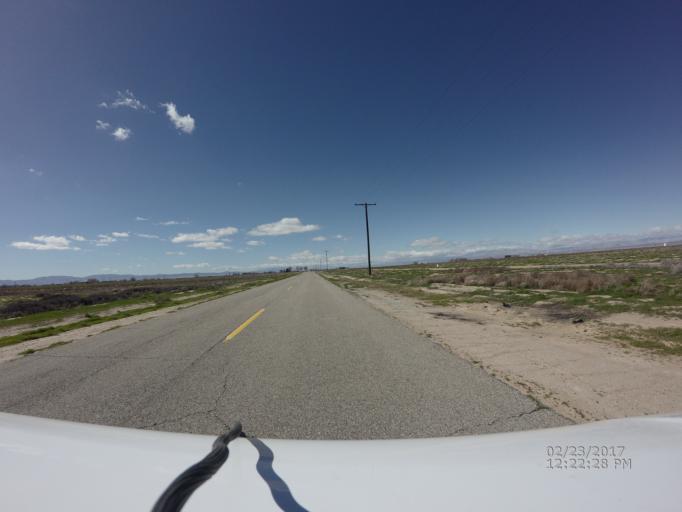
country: US
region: California
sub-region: Los Angeles County
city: Lancaster
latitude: 34.7489
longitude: -117.9897
